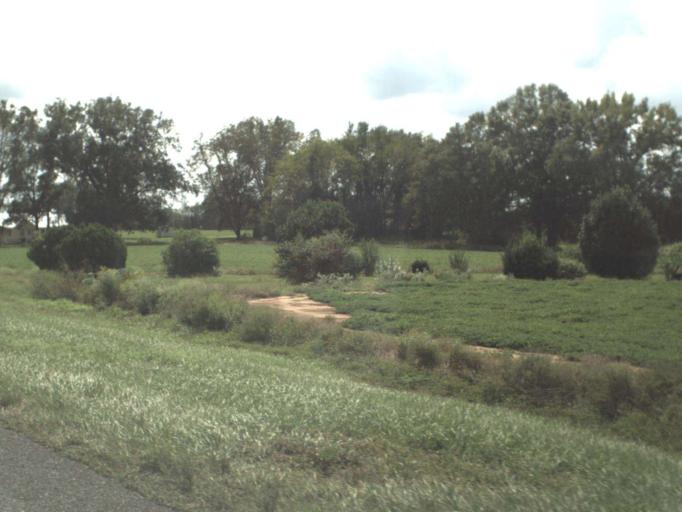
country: US
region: Florida
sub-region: Jackson County
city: Marianna
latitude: 30.8699
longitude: -85.3598
